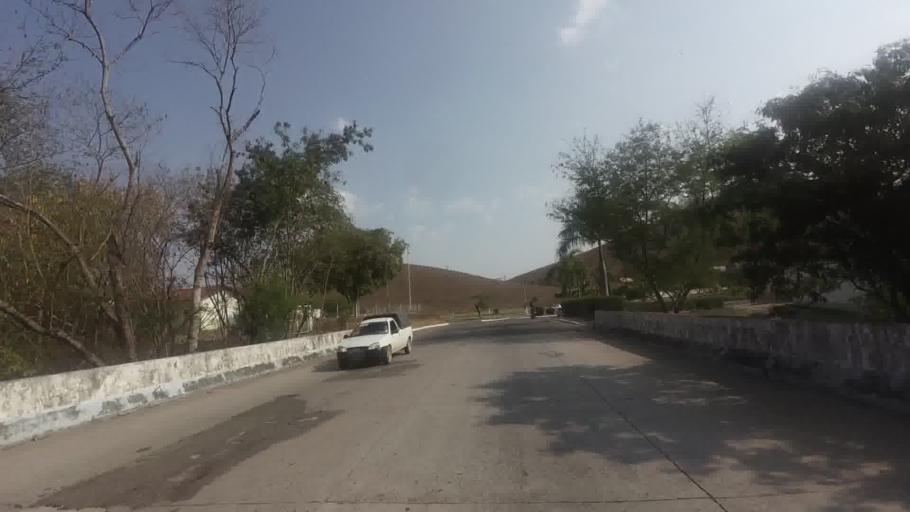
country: BR
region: Rio de Janeiro
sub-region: Bom Jesus Do Itabapoana
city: Bom Jesus do Itabapoana
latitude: -21.1350
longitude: -41.6614
